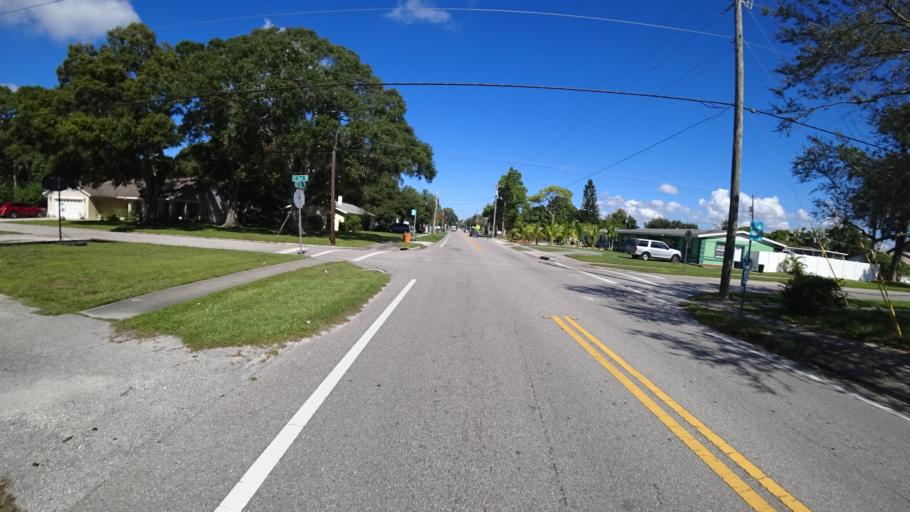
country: US
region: Florida
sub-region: Manatee County
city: West Bradenton
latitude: 27.4901
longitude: -82.6040
